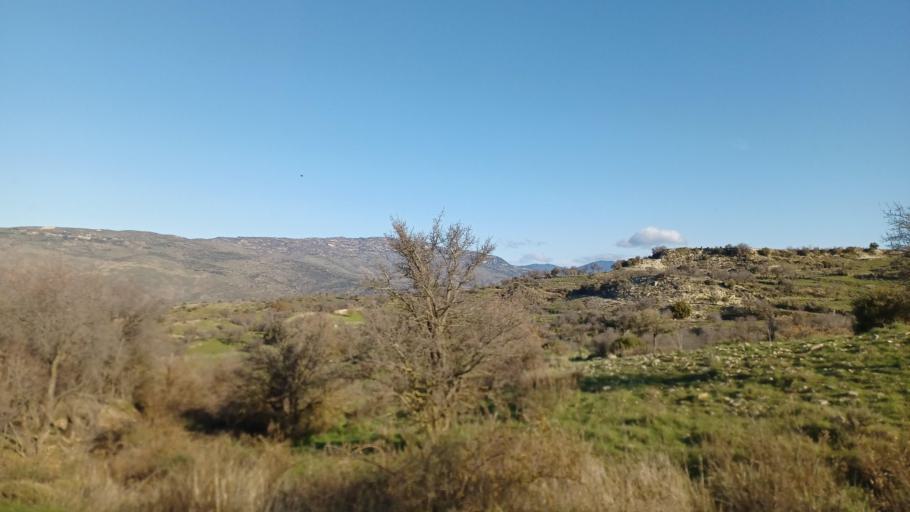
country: CY
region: Limassol
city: Pachna
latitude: 34.8153
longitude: 32.6555
